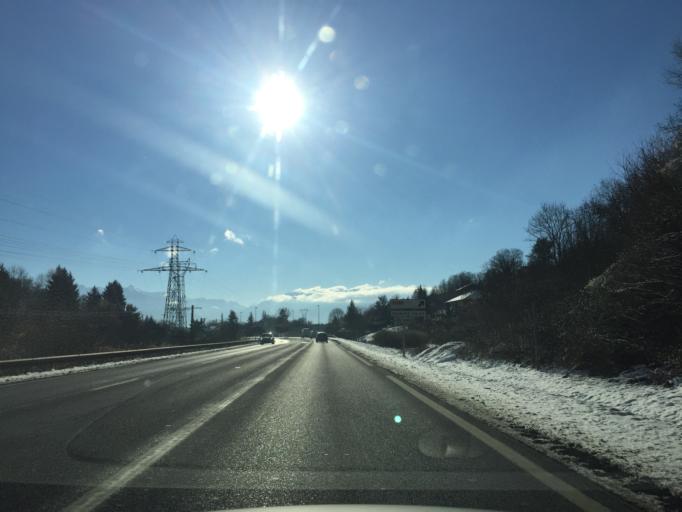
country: FR
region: Rhone-Alpes
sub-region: Departement de la Haute-Savoie
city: Cranves-Sales
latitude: 46.1931
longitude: 6.2926
